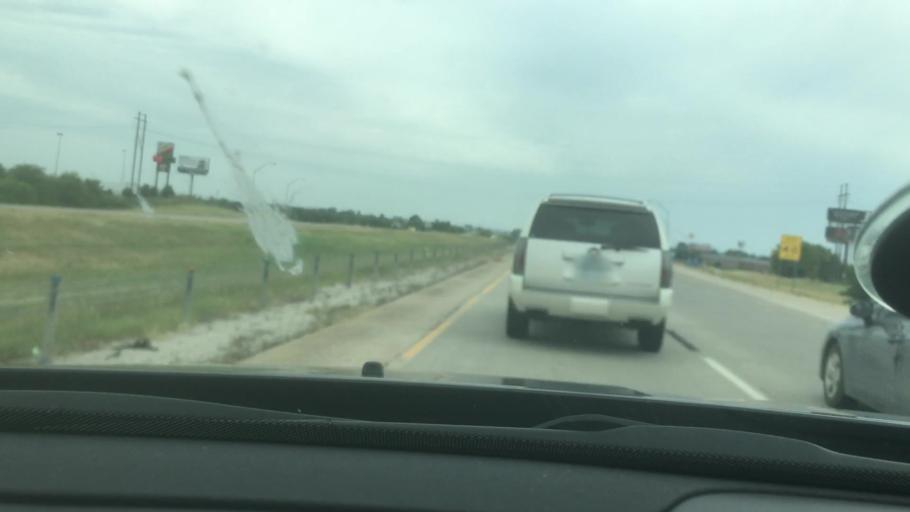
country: US
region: Oklahoma
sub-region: Carter County
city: Ardmore
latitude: 34.1975
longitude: -97.1638
